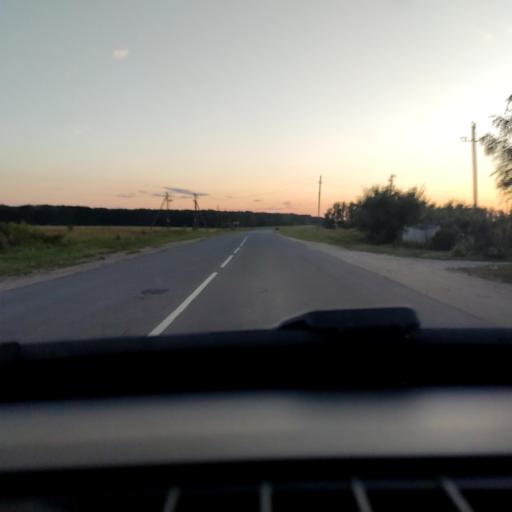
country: RU
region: Lipetsk
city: Zadonsk
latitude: 52.2962
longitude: 38.8446
